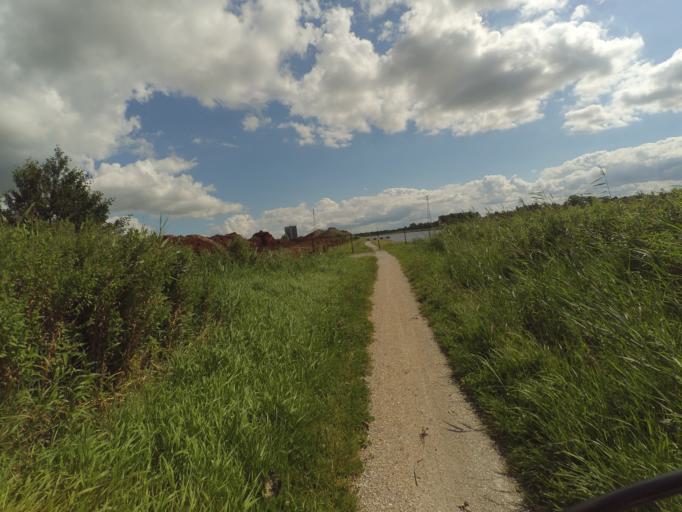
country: NL
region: Friesland
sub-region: Gemeente Achtkarspelen
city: Kootstertille
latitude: 53.2029
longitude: 6.0810
